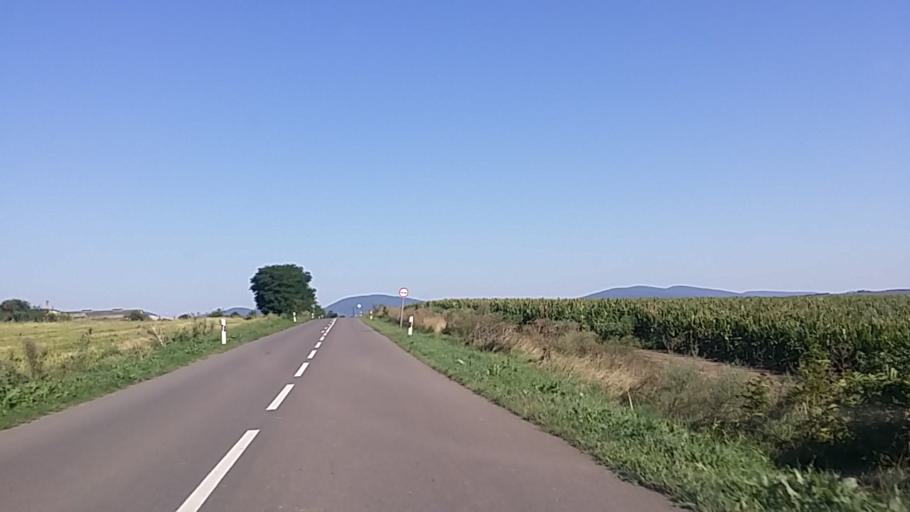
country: HU
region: Nograd
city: Jobbagyi
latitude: 47.8505
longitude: 19.6298
